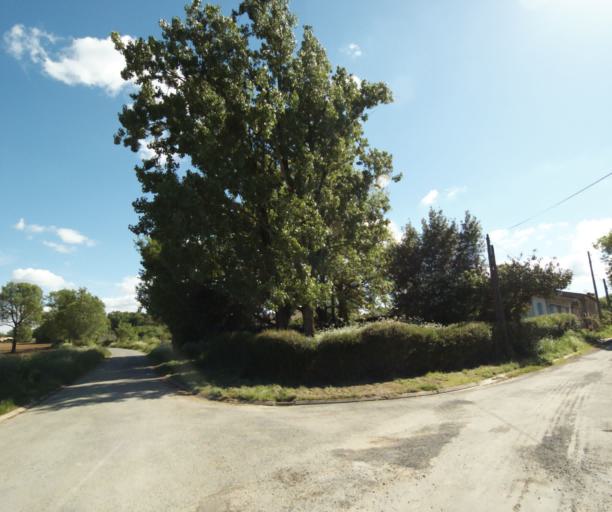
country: FR
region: Poitou-Charentes
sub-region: Departement de la Charente-Maritime
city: Saint-Georges-des-Coteaux
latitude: 45.7784
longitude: -0.6955
